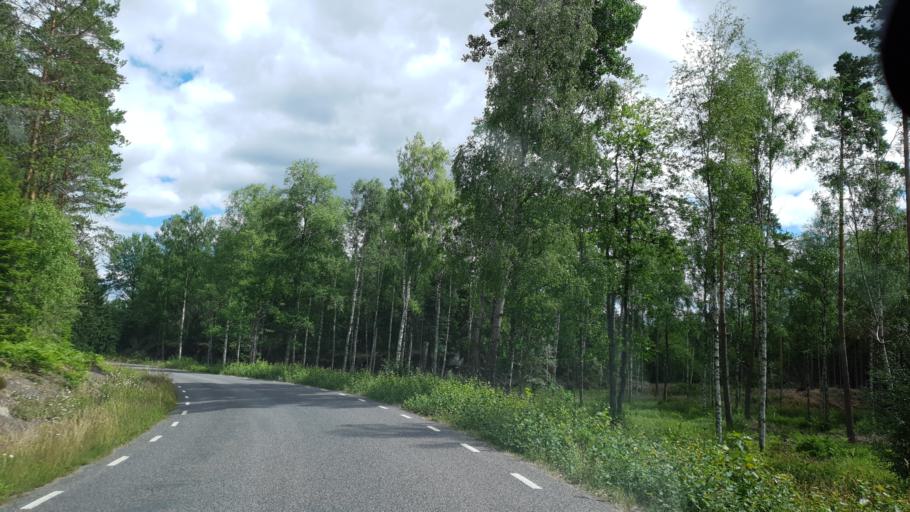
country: SE
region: Kronoberg
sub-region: Uppvidinge Kommun
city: Aseda
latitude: 57.1939
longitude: 15.4199
